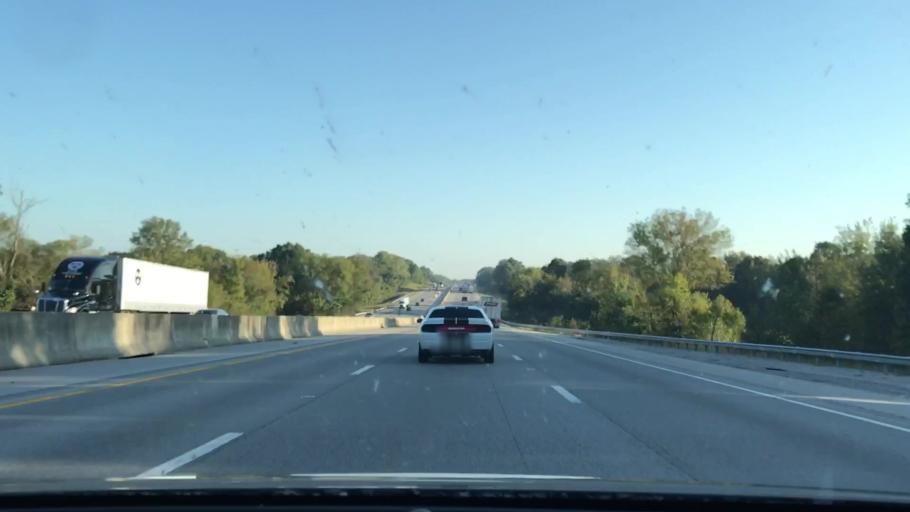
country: US
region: Kentucky
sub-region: Simpson County
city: Franklin
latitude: 36.7686
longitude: -86.4833
